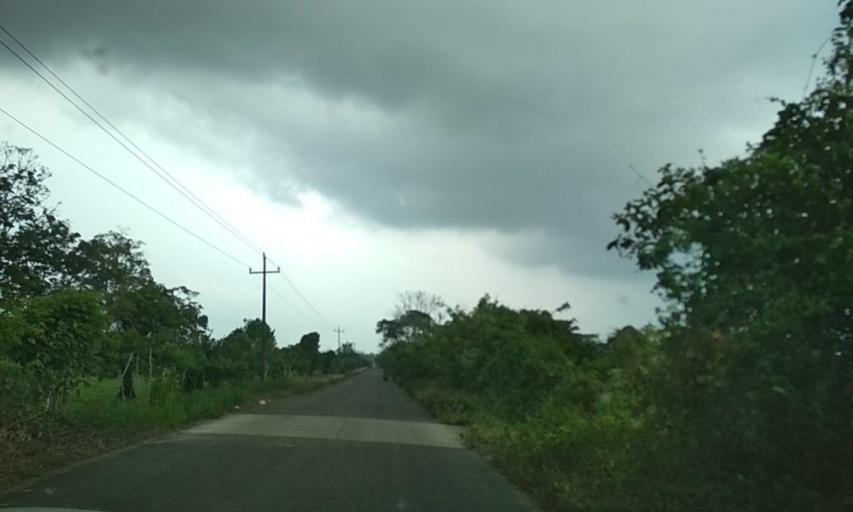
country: MX
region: Tabasco
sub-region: Huimanguillo
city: Francisco Rueda
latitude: 17.5538
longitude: -94.1227
